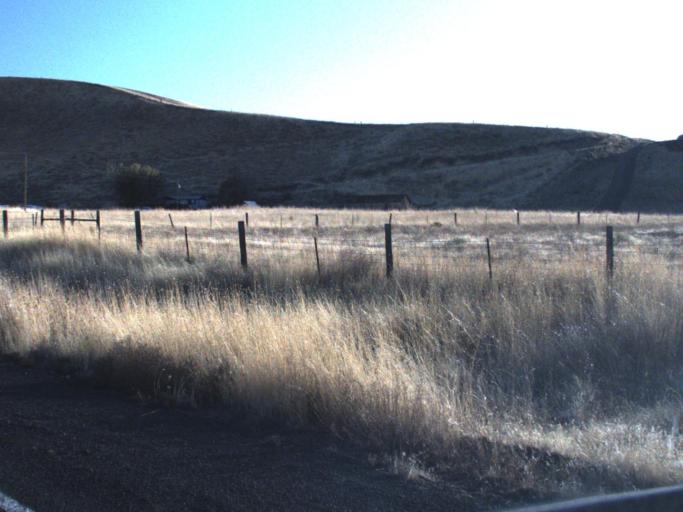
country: US
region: Washington
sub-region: Walla Walla County
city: Waitsburg
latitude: 46.6486
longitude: -118.2552
